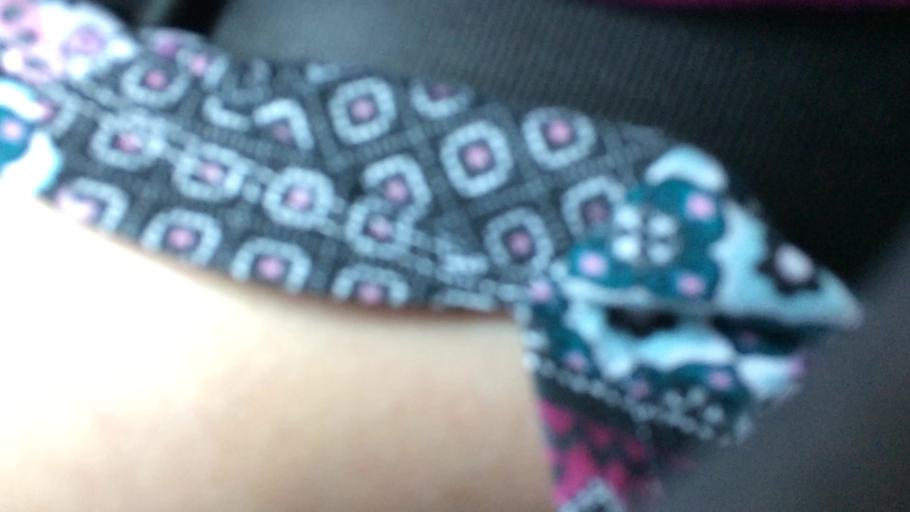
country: US
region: New Mexico
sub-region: Colfax County
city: Springer
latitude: 36.3345
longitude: -104.6146
